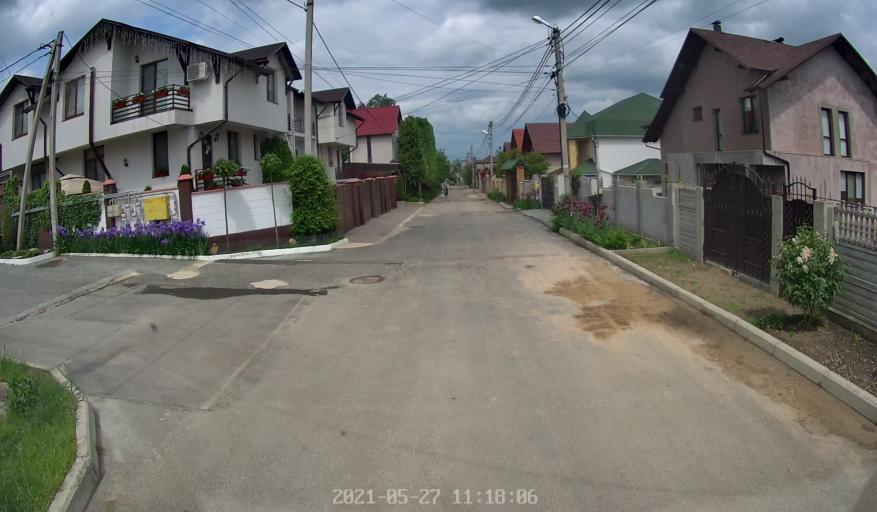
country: MD
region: Chisinau
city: Stauceni
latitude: 47.1065
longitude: 28.8680
